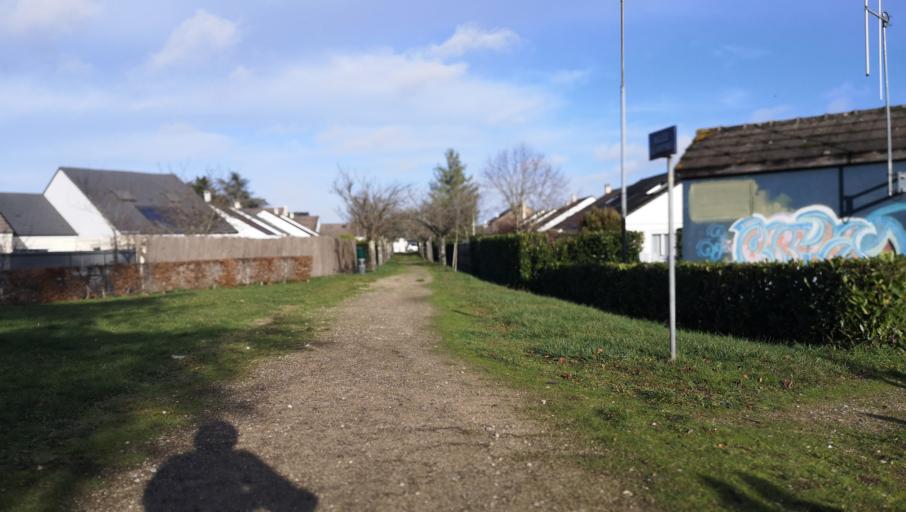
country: FR
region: Centre
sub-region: Departement du Loiret
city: Saint-Pryve-Saint-Mesmin
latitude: 47.8762
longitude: 1.8718
